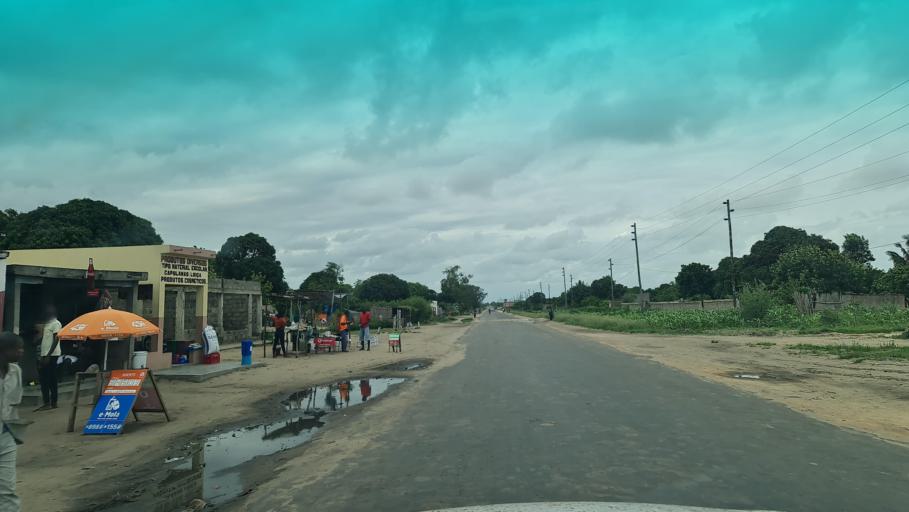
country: MZ
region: Maputo
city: Manhica
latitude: -25.4411
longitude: 32.7735
